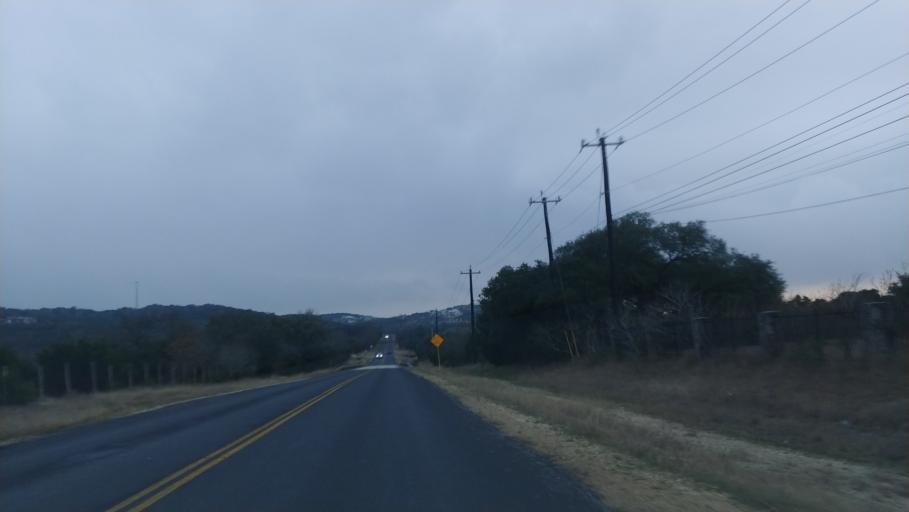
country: US
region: Texas
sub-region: Bexar County
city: Cross Mountain
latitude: 29.6755
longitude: -98.6748
